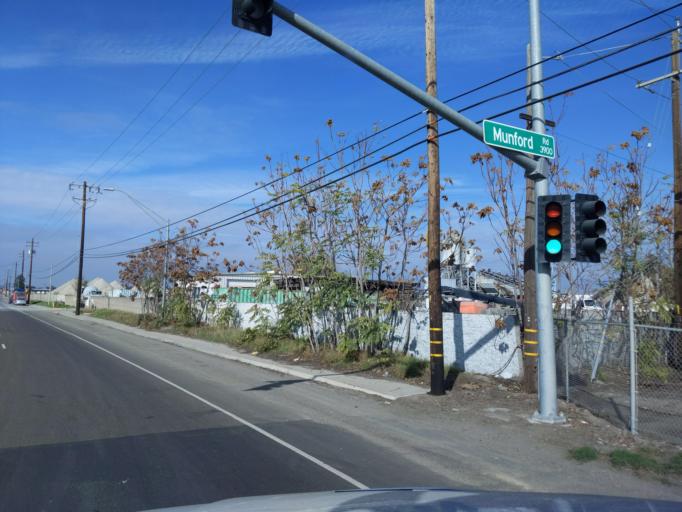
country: US
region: California
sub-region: San Joaquin County
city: Kennedy
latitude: 37.9308
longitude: -121.2246
